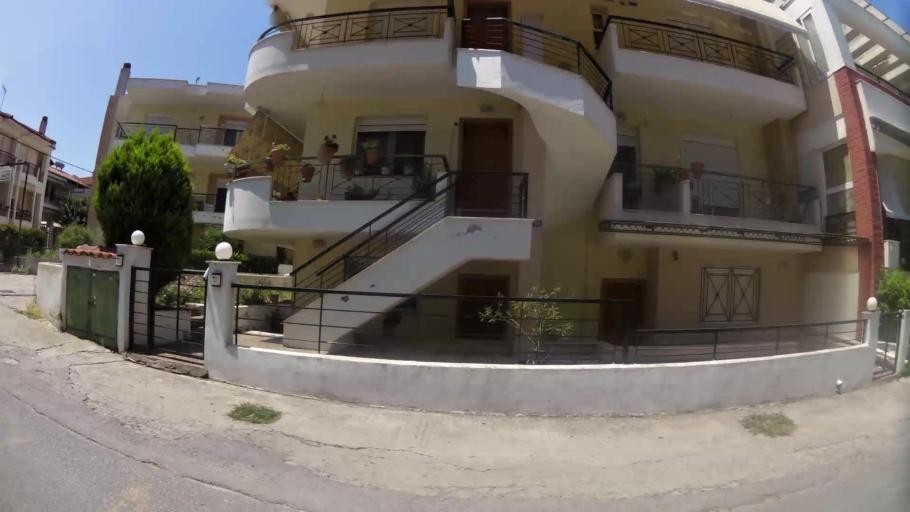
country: GR
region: Central Macedonia
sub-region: Nomos Thessalonikis
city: Plagiari
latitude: 40.4725
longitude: 22.9585
